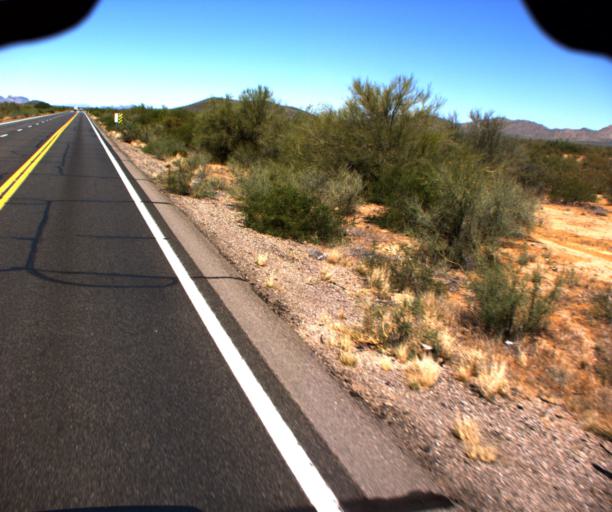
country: US
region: Arizona
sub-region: Yavapai County
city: Congress
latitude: 34.1514
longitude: -112.9908
